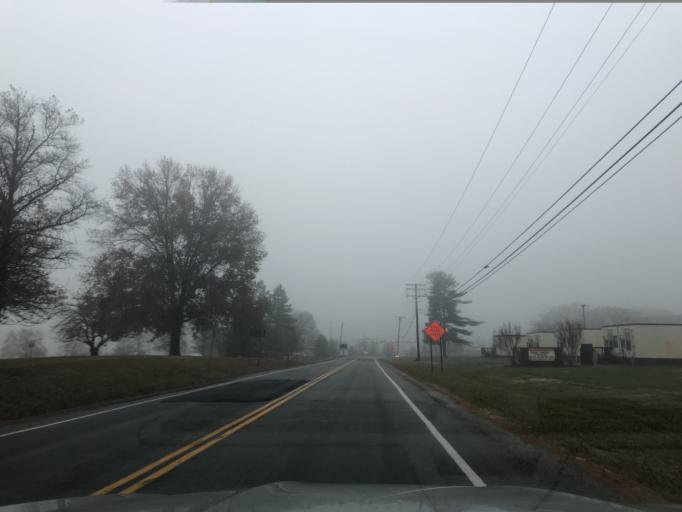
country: US
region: Maryland
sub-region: Harford County
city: South Bel Air
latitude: 39.5576
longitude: -76.2864
